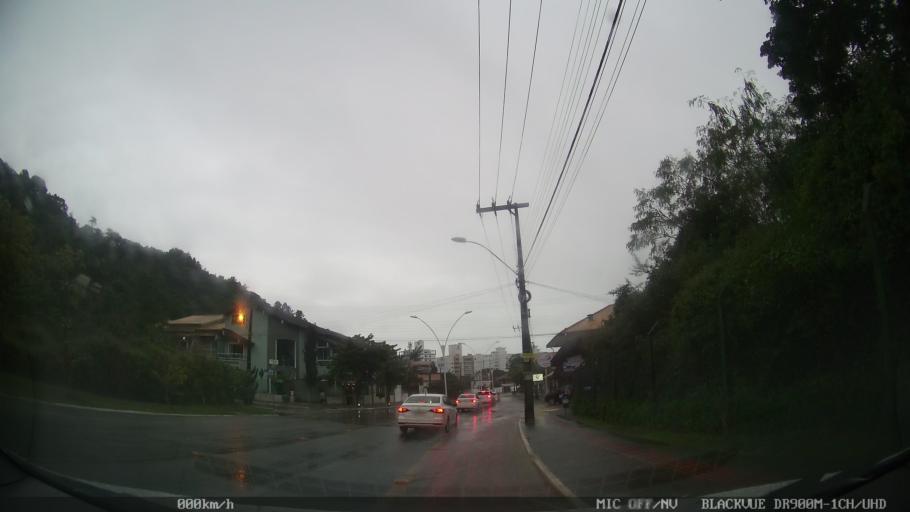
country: BR
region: Santa Catarina
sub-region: Balneario Camboriu
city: Balneario Camboriu
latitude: -26.9619
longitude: -48.6315
